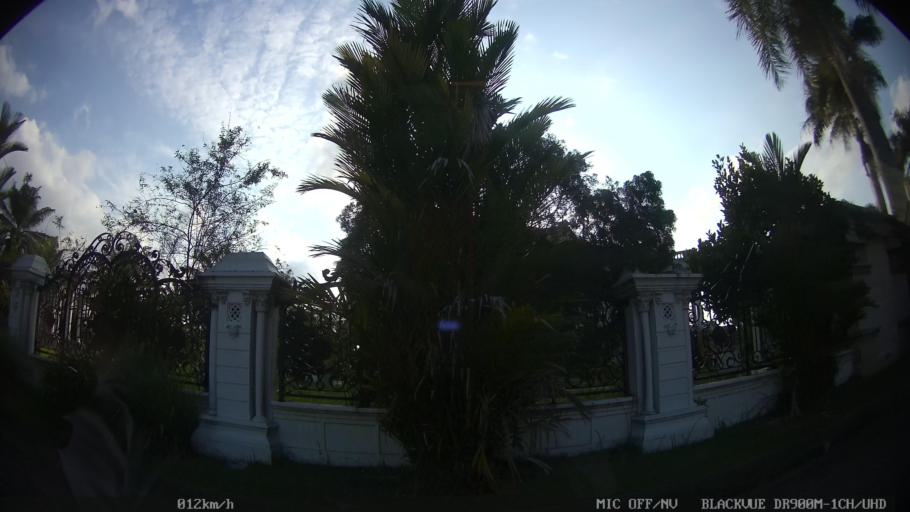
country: ID
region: North Sumatra
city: Medan
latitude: 3.6223
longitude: 98.6533
